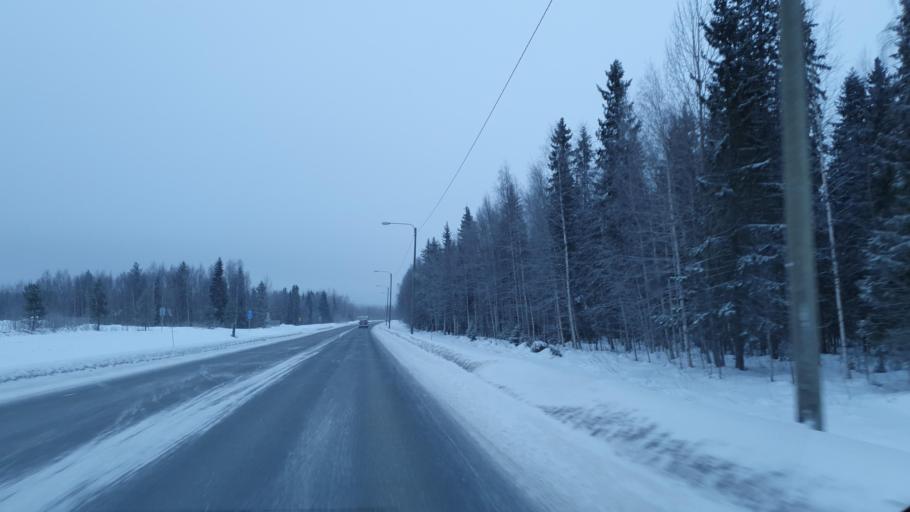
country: FI
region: Lapland
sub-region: Torniolaakso
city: Ylitornio
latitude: 66.3505
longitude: 23.6899
